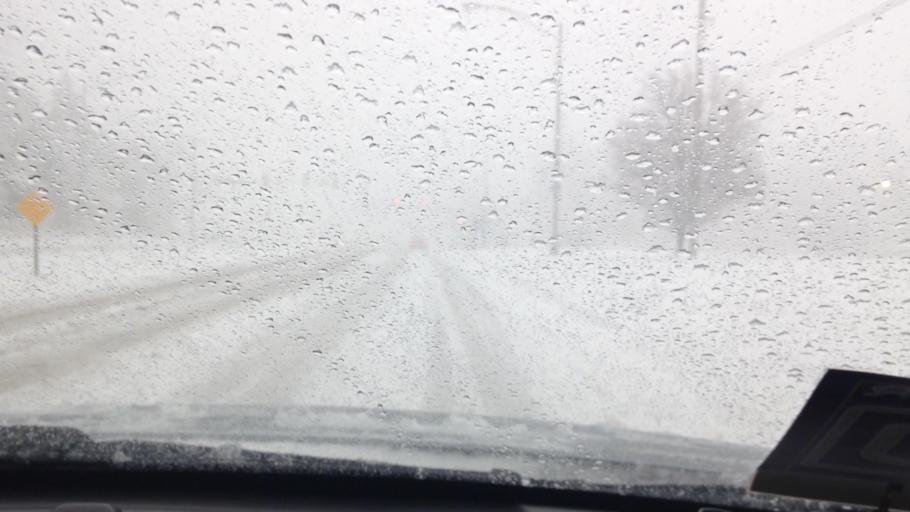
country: US
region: Kansas
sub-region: Johnson County
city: Shawnee
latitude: 39.1166
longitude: -94.7112
